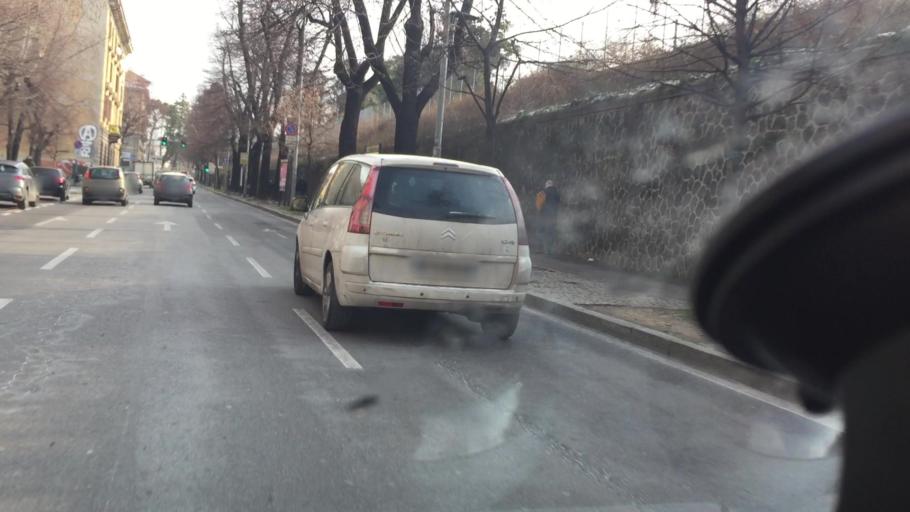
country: IT
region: Lombardy
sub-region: Provincia di Bergamo
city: Bergamo
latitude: 45.6894
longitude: 9.6713
